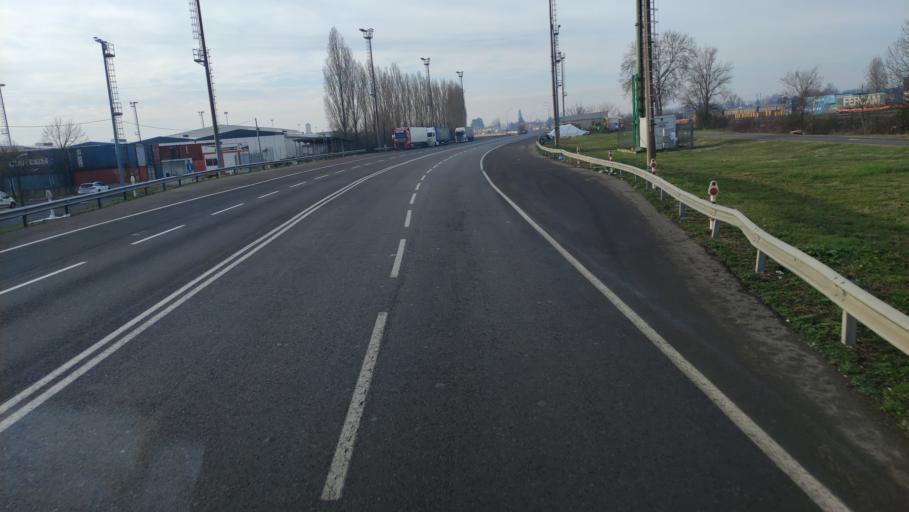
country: IT
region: Emilia-Romagna
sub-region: Provincia di Bologna
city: San Giorgio di Piano
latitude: 44.6242
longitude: 11.3790
